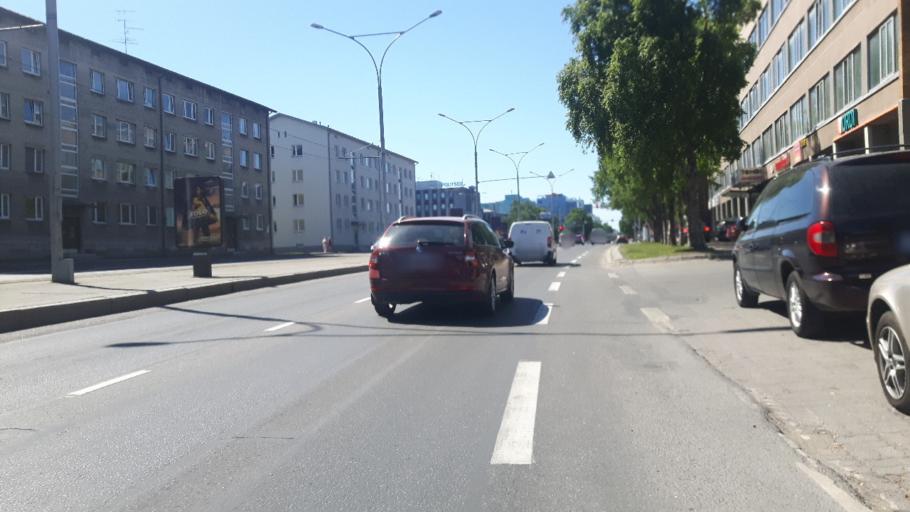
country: EE
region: Harju
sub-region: Tallinna linn
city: Tallinn
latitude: 59.4114
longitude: 24.7377
